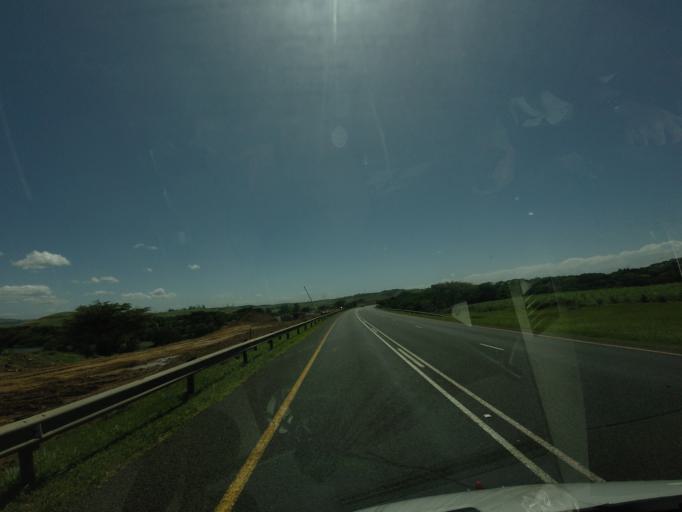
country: ZA
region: KwaZulu-Natal
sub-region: uThungulu District Municipality
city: eSikhawini
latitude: -28.9335
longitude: 31.7551
